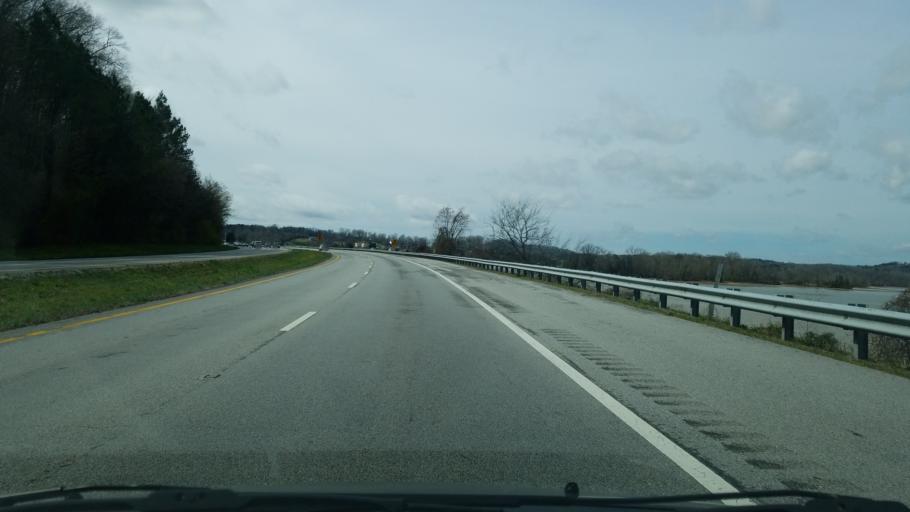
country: US
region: Tennessee
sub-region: Hamilton County
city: Harrison
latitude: 35.1427
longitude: -85.1178
